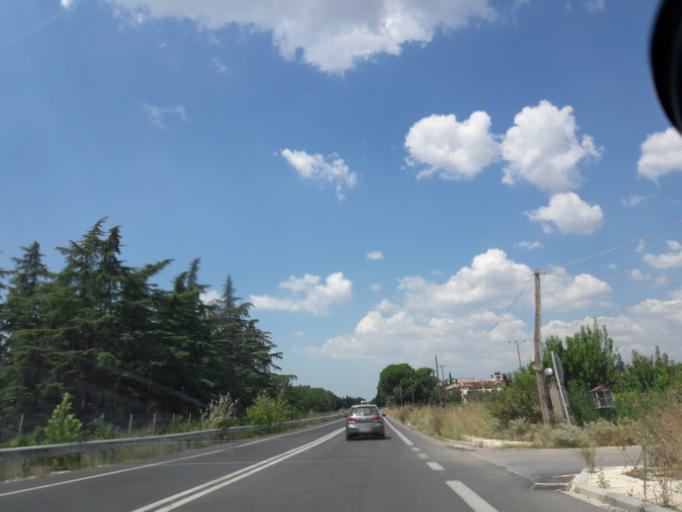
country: GR
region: Central Macedonia
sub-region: Nomos Thessalonikis
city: Souroti
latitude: 40.5083
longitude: 23.0861
